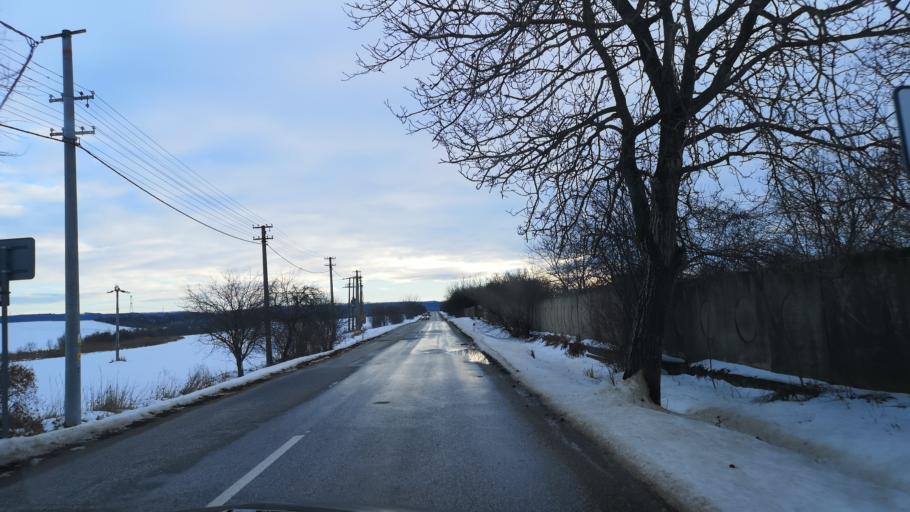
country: SK
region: Nitriansky
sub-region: Okres Nitra
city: Vrable
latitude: 48.1307
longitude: 18.3354
